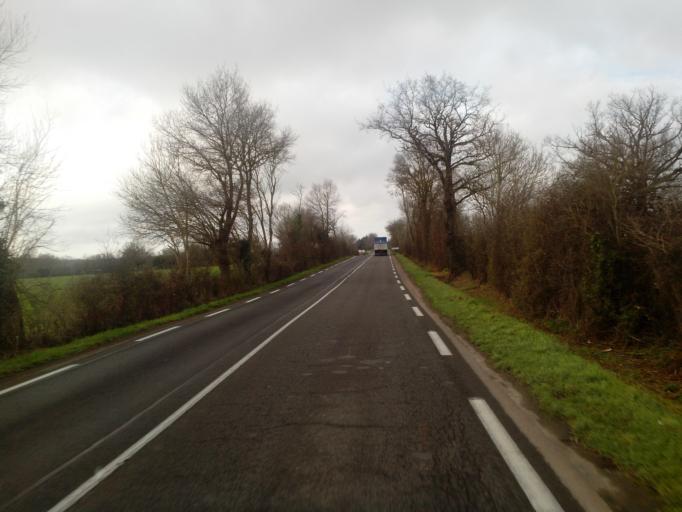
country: FR
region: Poitou-Charentes
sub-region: Departement des Deux-Sevres
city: Chiche
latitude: 46.8022
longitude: -0.3700
